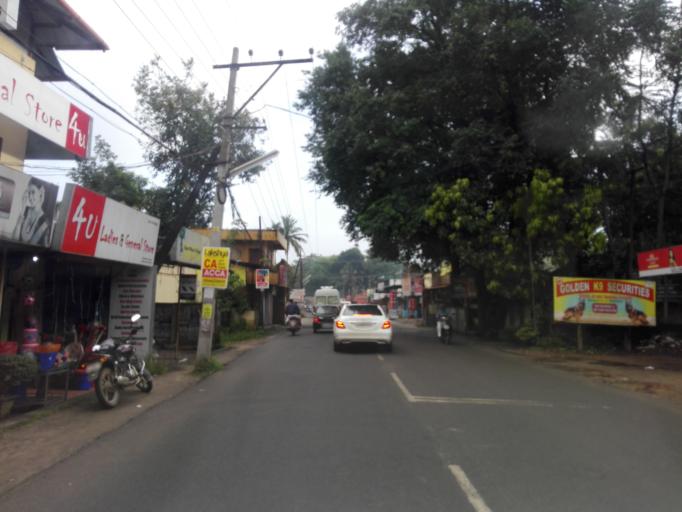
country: IN
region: Kerala
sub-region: Alappuzha
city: Arukutti
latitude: 9.9144
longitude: 76.3636
